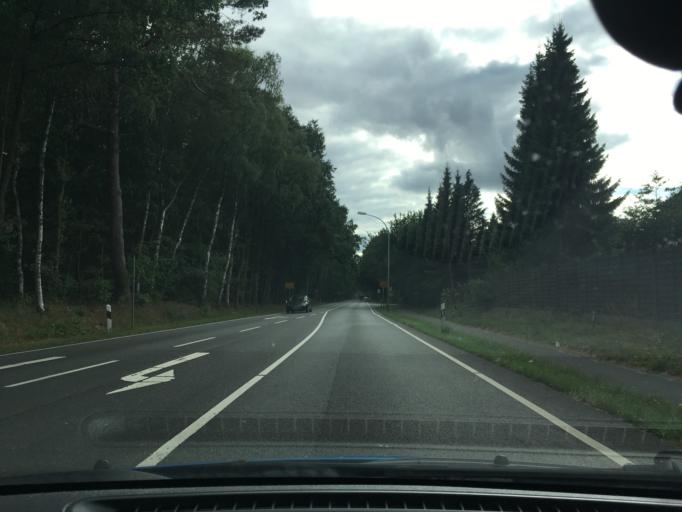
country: DE
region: Lower Saxony
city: Neu Wulmstorf
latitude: 53.4581
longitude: 9.7818
